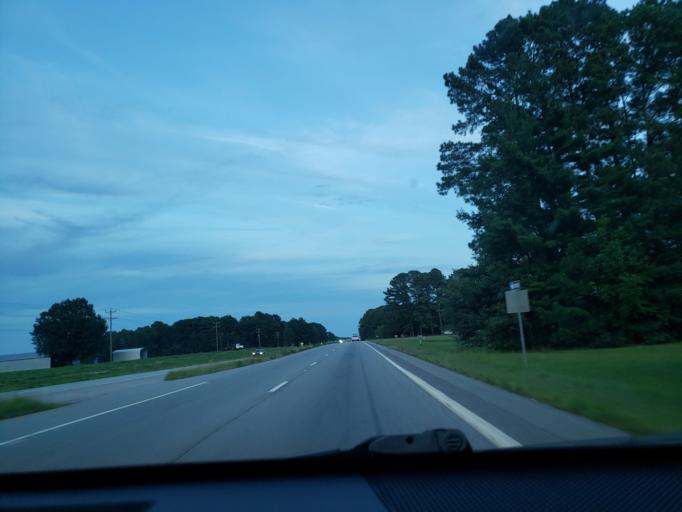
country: US
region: Virginia
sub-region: Southampton County
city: Courtland
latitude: 36.7041
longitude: -77.1178
